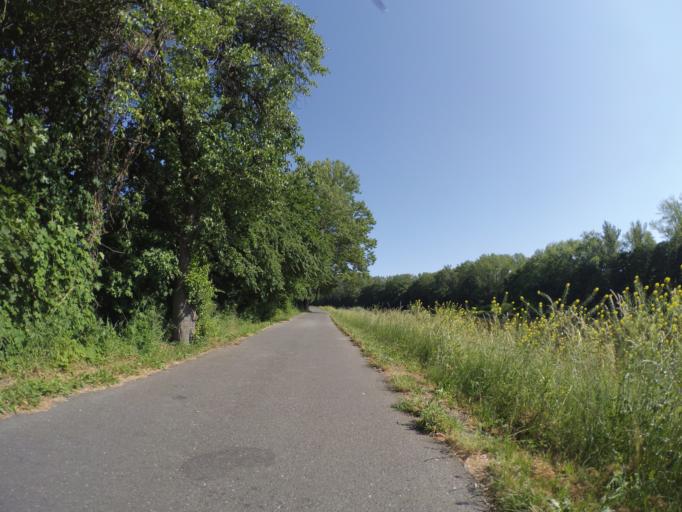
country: CZ
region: Central Bohemia
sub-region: Okres Nymburk
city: Podebrady
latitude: 50.1635
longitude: 15.0933
